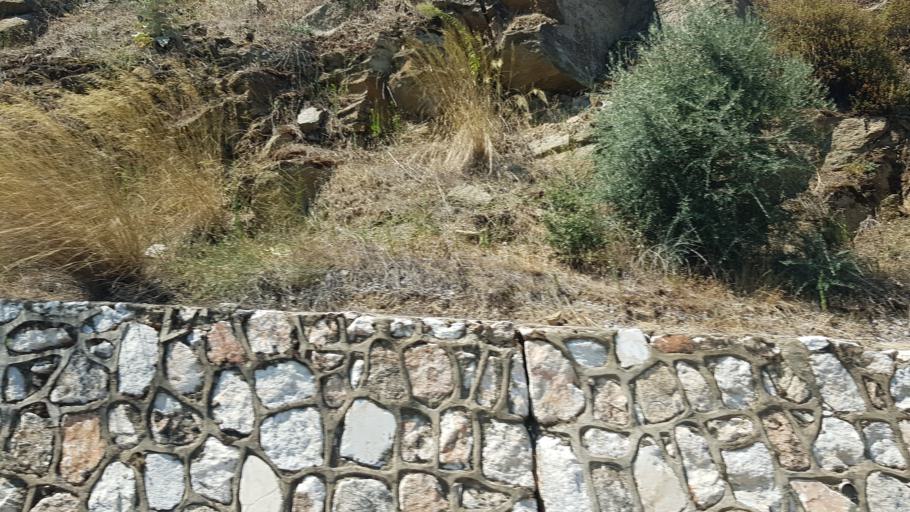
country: TR
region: Aydin
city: Akcaova
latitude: 37.5091
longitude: 28.1013
